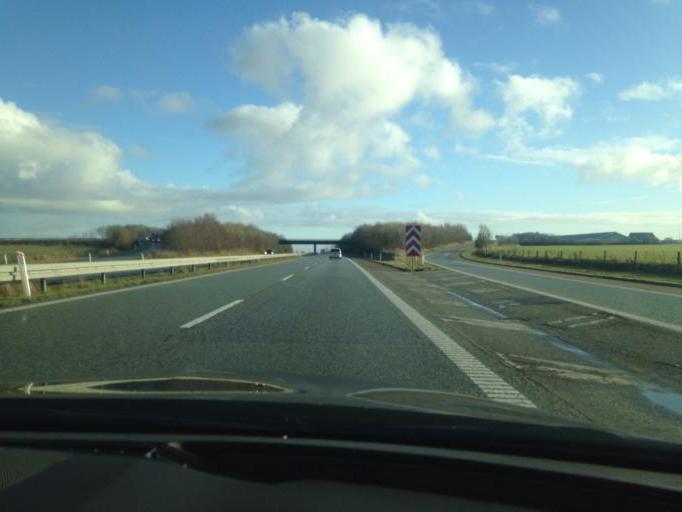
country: DK
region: South Denmark
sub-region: Vejen Kommune
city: Brorup
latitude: 55.5048
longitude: 9.0161
